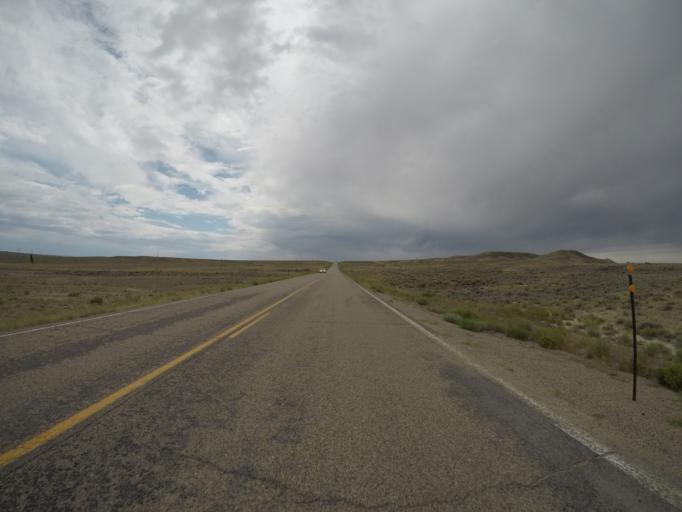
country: US
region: Wyoming
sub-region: Lincoln County
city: Kemmerer
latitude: 41.9731
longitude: -110.0798
